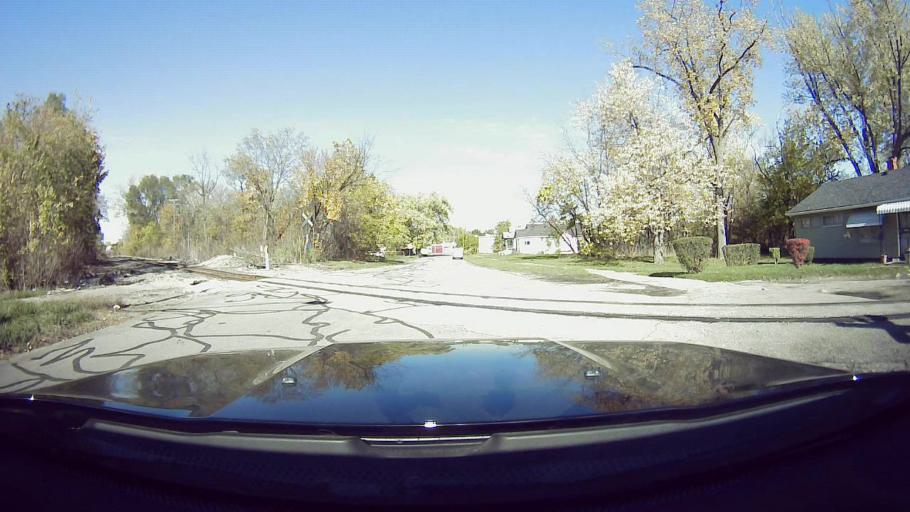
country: US
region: Michigan
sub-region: Wayne County
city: Dearborn
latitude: 42.3769
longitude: -83.1635
